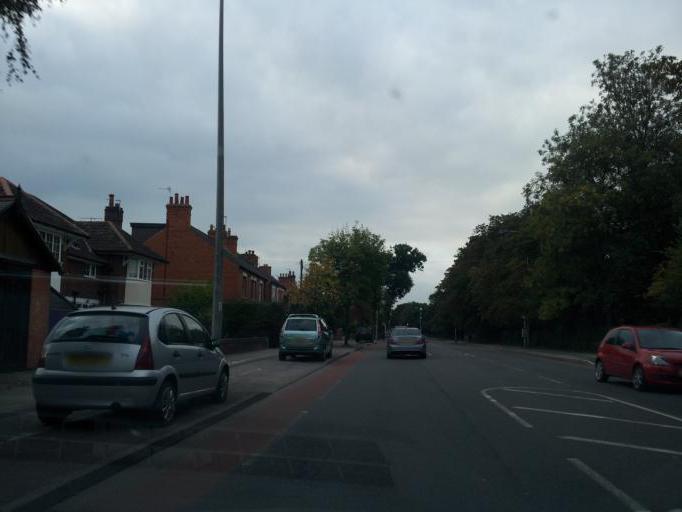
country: GB
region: England
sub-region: Nottinghamshire
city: Newark on Trent
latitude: 53.0649
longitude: -0.7913
